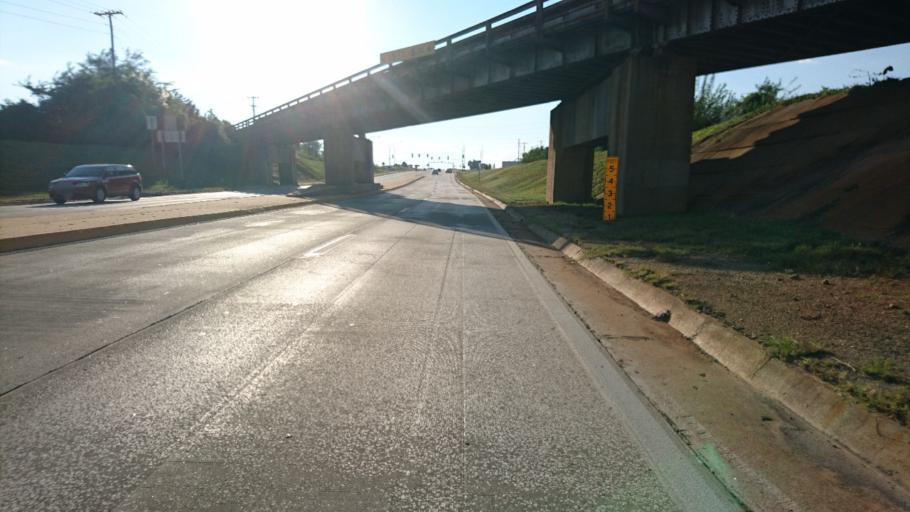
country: US
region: Missouri
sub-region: Greene County
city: Springfield
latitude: 37.2126
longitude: -93.3779
